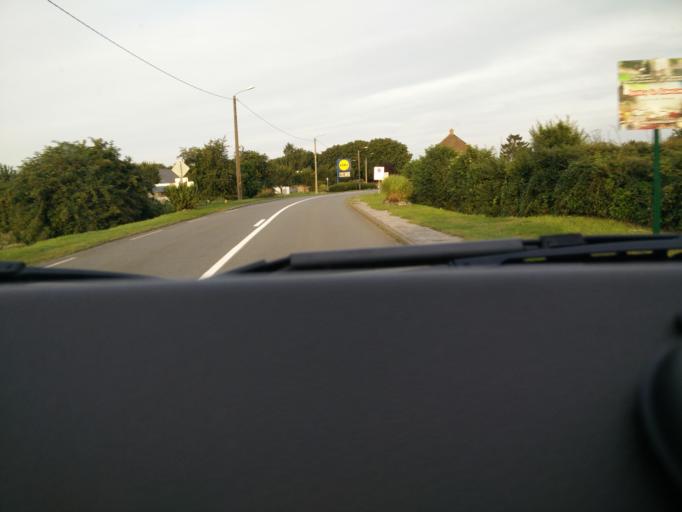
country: FR
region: Nord-Pas-de-Calais
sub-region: Departement du Nord
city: Bavay
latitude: 50.3010
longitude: 3.7877
